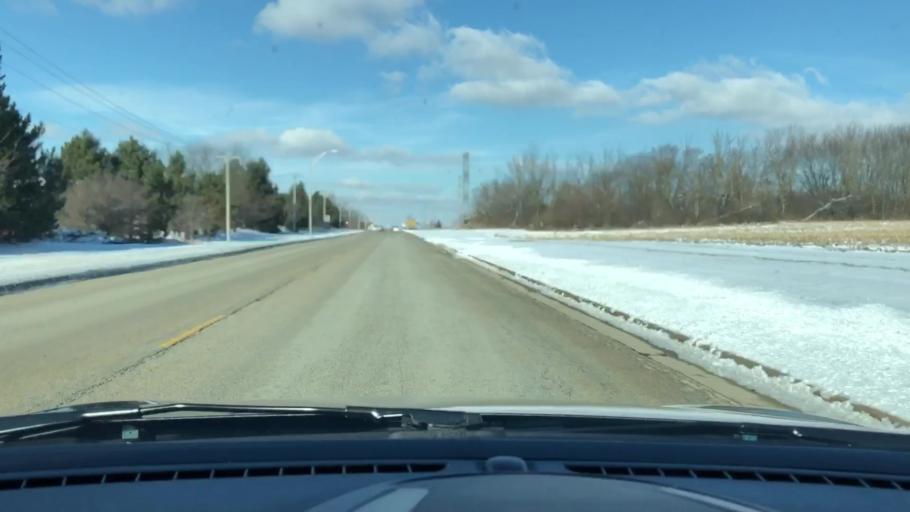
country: US
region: Illinois
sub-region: Will County
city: Mokena
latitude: 41.4883
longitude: -87.8879
